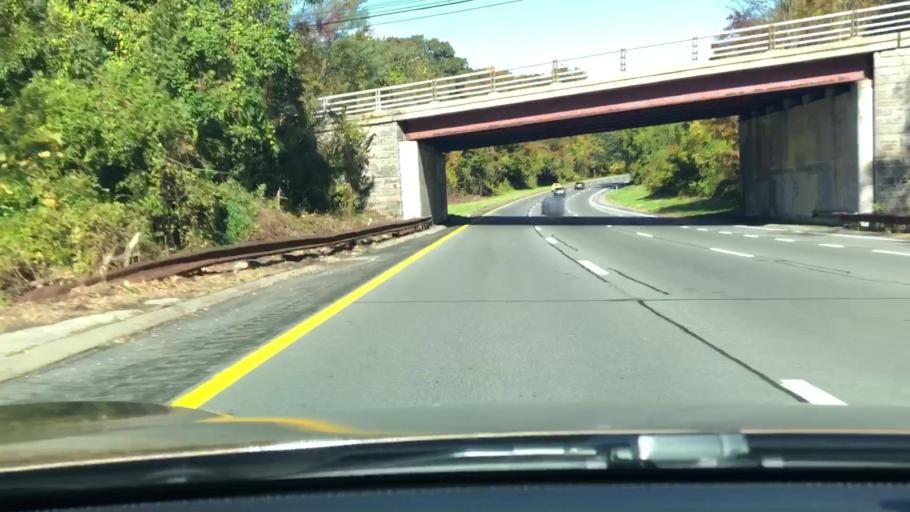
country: US
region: New York
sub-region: Westchester County
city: Greenville
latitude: 40.9880
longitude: -73.8389
